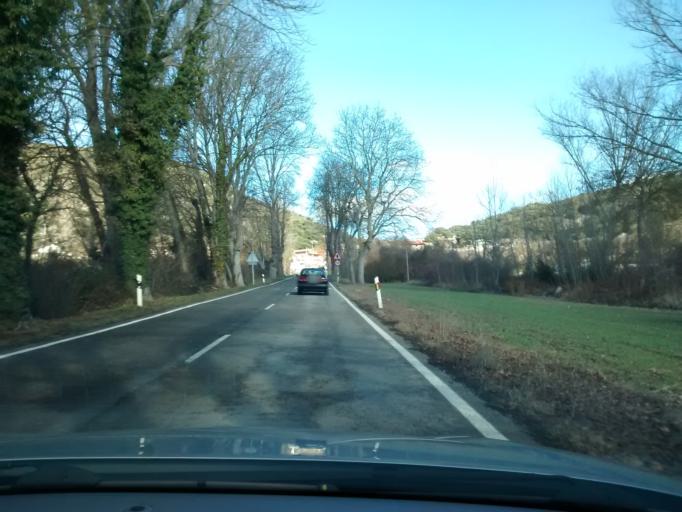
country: ES
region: Castille and Leon
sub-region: Provincia de Burgos
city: Medina de Pomar
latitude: 42.8902
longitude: -3.5947
